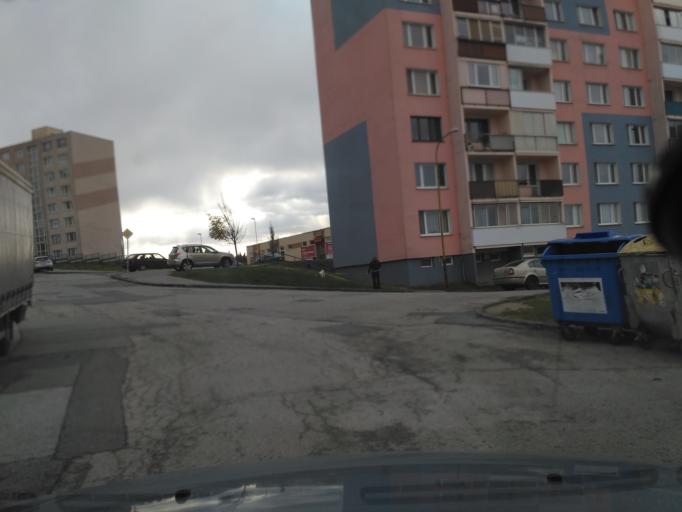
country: SK
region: Kosicky
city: Kosice
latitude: 48.7323
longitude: 21.2815
